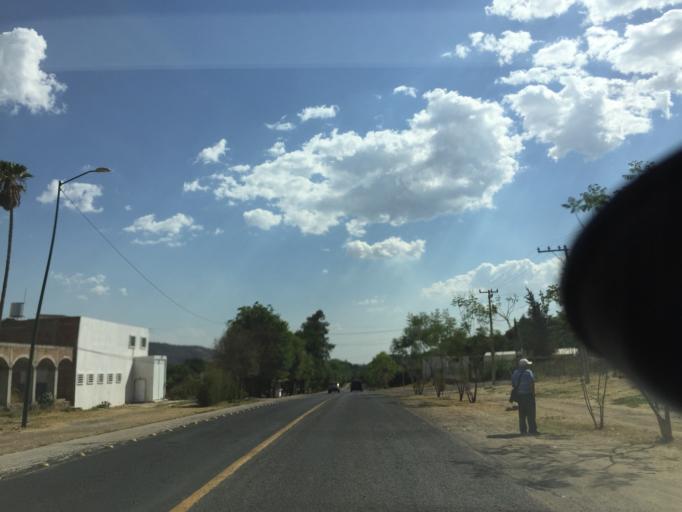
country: MX
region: Jalisco
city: Atotonilco el Alto
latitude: 20.5602
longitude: -102.4863
